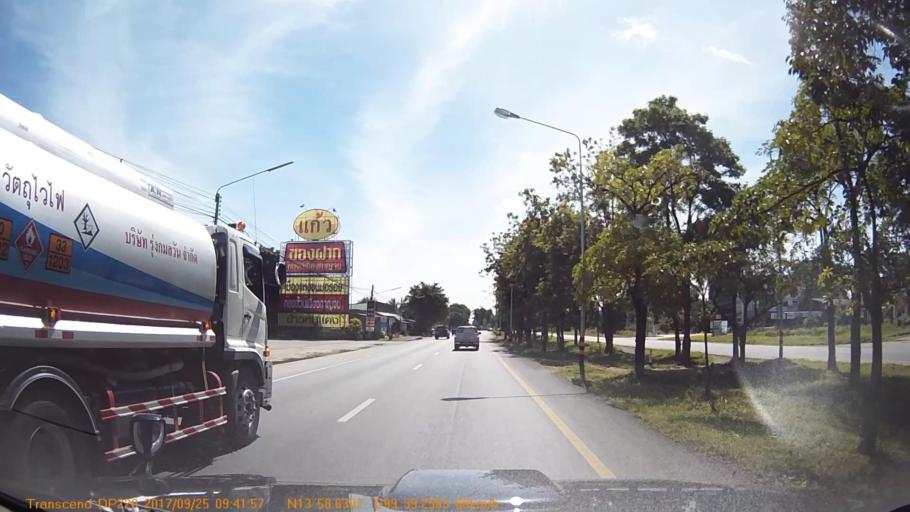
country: TH
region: Kanchanaburi
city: Tha Muang
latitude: 13.9771
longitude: 99.6545
